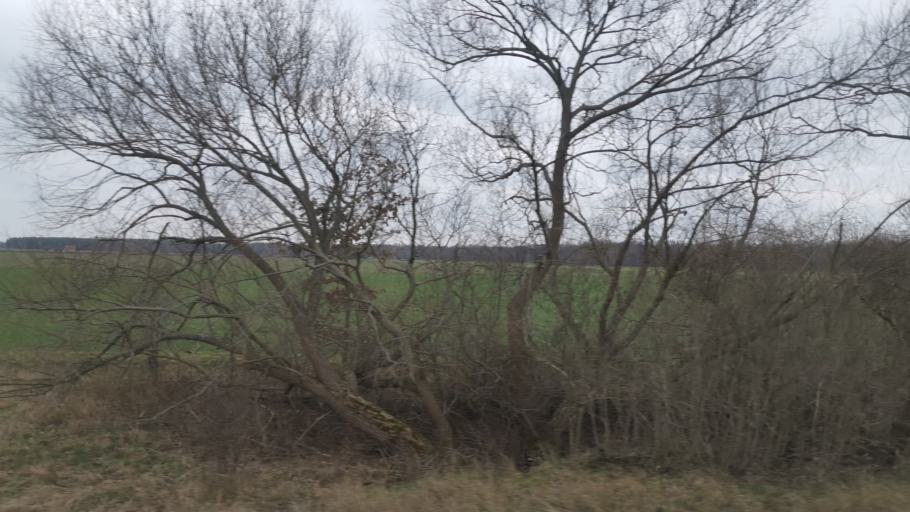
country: DE
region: Brandenburg
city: Doberlug-Kirchhain
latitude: 51.6366
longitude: 13.5716
